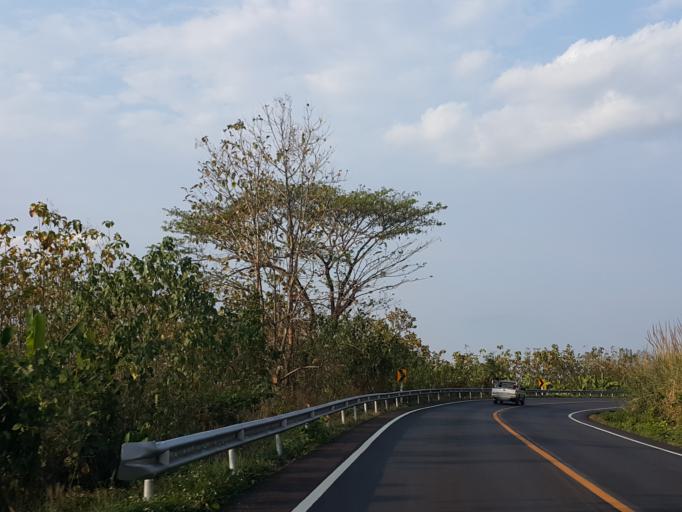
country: TH
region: Lampang
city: Lampang
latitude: 18.4707
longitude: 99.4636
